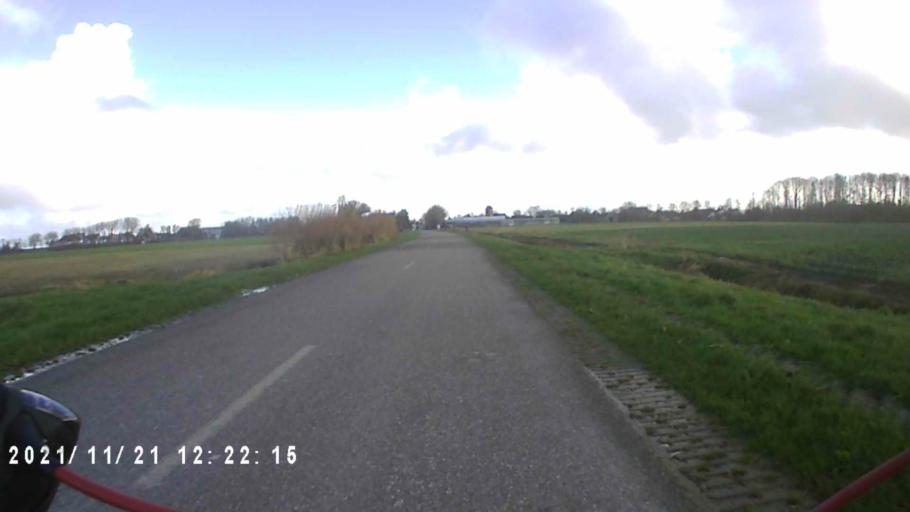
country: NL
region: Friesland
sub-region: Gemeente Dongeradeel
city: Ternaard
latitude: 53.3935
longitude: 6.0406
